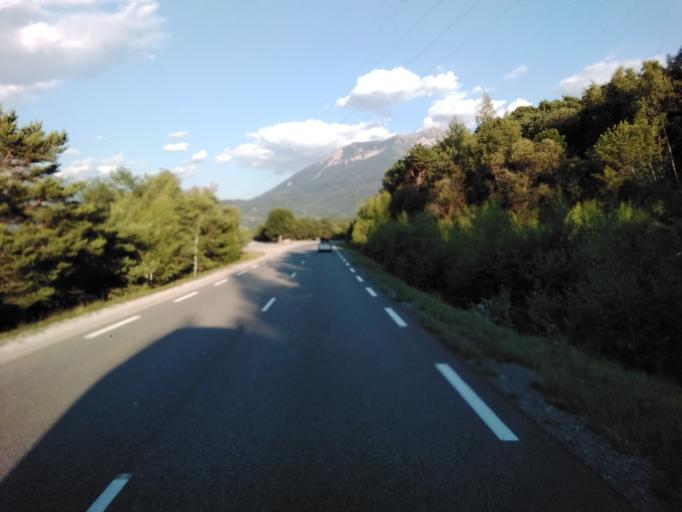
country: FR
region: Provence-Alpes-Cote d'Azur
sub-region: Departement des Hautes-Alpes
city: Chorges
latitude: 44.4551
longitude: 6.3153
